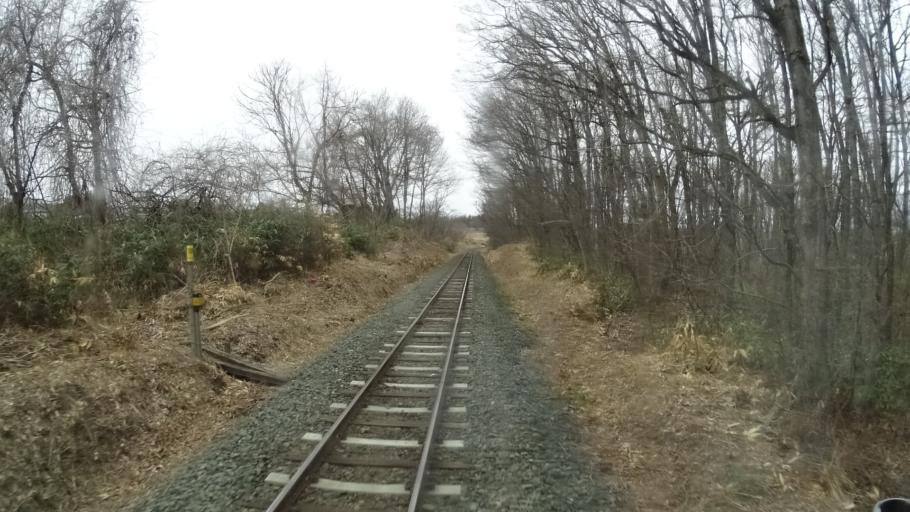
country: JP
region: Iwate
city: Hanamaki
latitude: 39.3922
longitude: 141.2164
